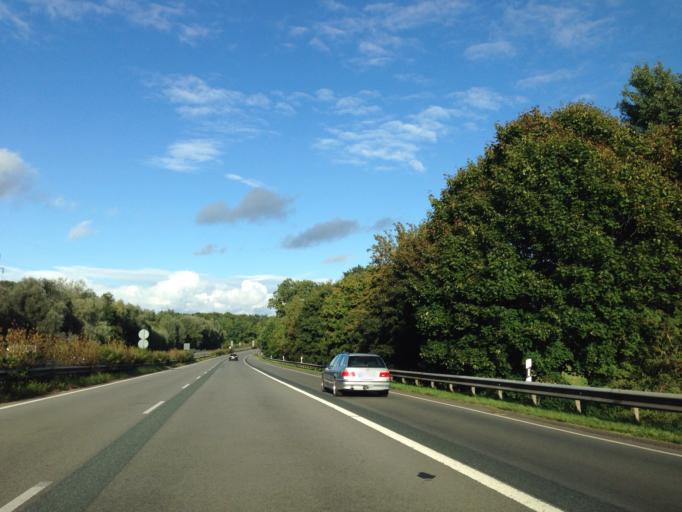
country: DE
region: Lower Saxony
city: Melbeck
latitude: 53.2050
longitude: 10.4080
